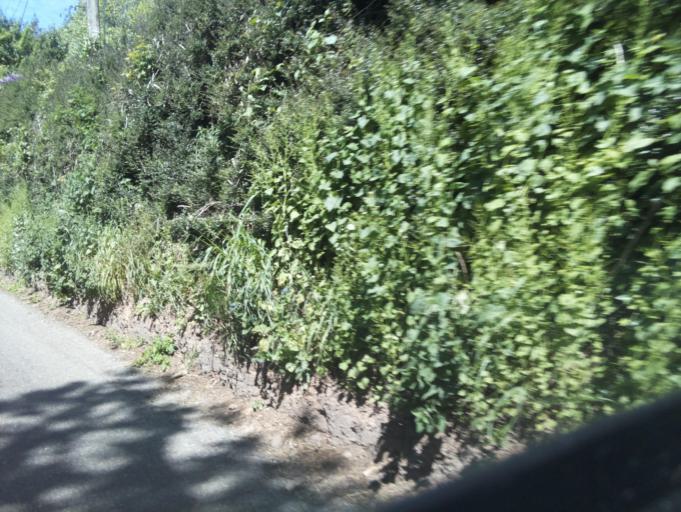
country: GB
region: England
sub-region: Devon
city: Honiton
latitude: 50.8153
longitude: -3.2492
